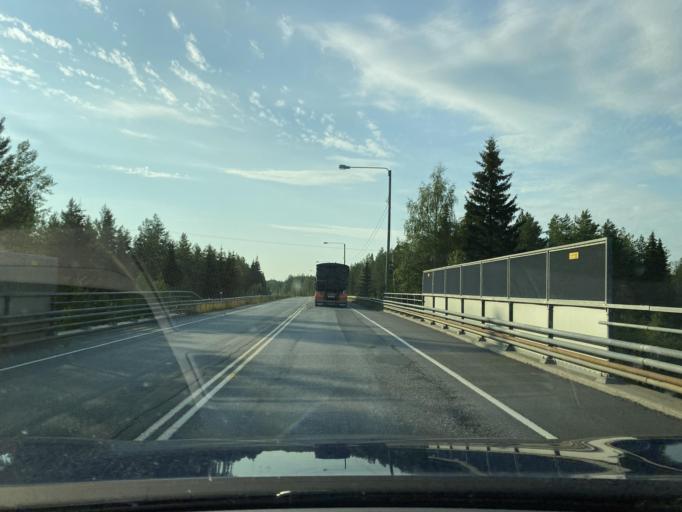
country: FI
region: Southern Ostrobothnia
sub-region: Seinaejoki
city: Kauhava
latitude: 63.0613
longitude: 23.0304
